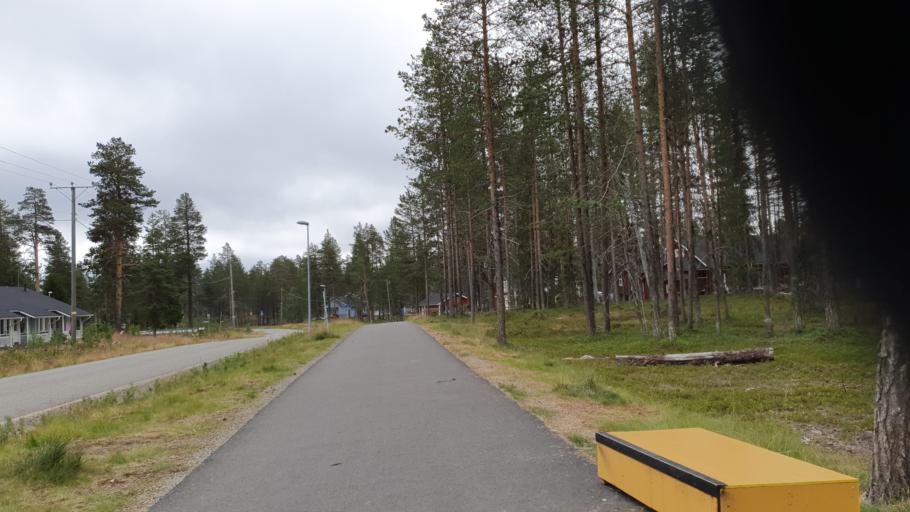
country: FI
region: Lapland
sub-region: Tunturi-Lappi
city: Kolari
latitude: 67.6244
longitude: 24.1473
